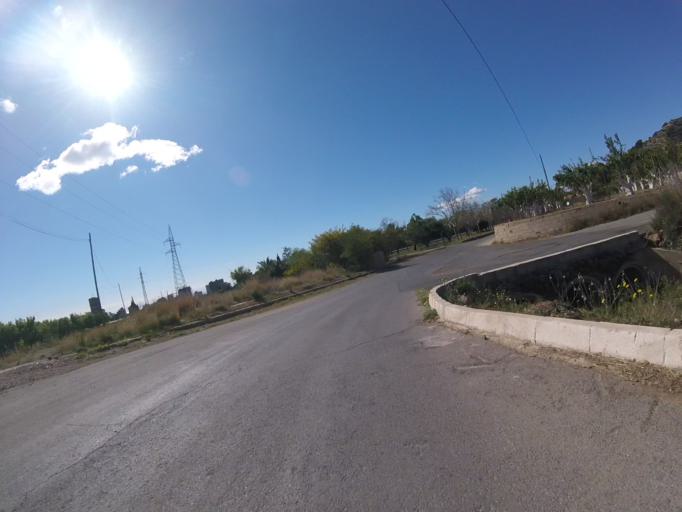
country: ES
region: Valencia
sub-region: Provincia de Castello
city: Benicassim
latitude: 40.0622
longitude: 0.0709
